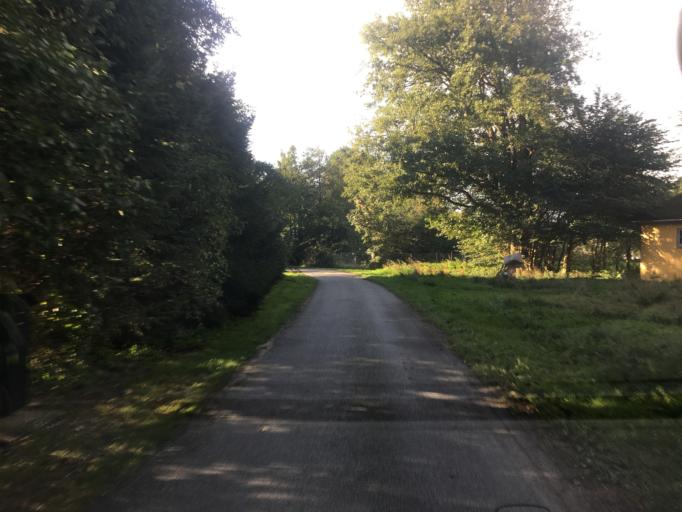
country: DE
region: Schleswig-Holstein
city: Ellhoft
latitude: 54.9631
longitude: 9.0114
